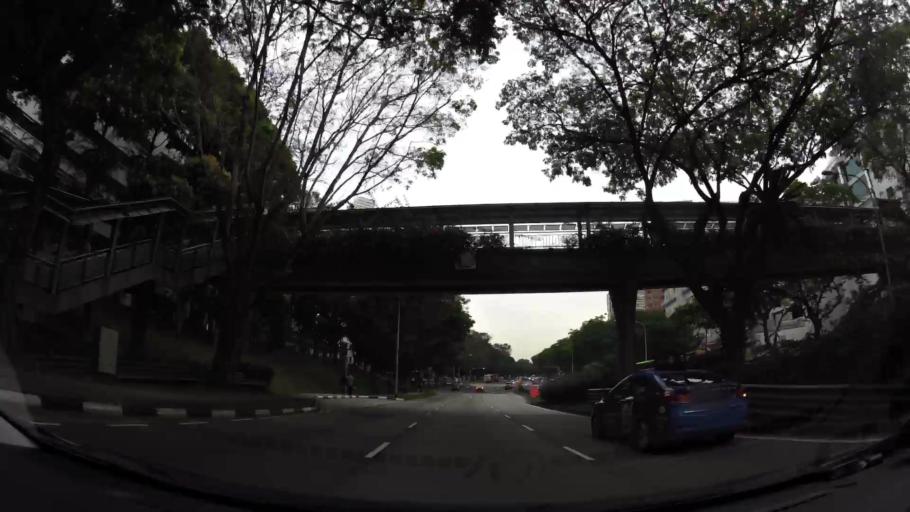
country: SG
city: Singapore
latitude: 1.3763
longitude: 103.8771
